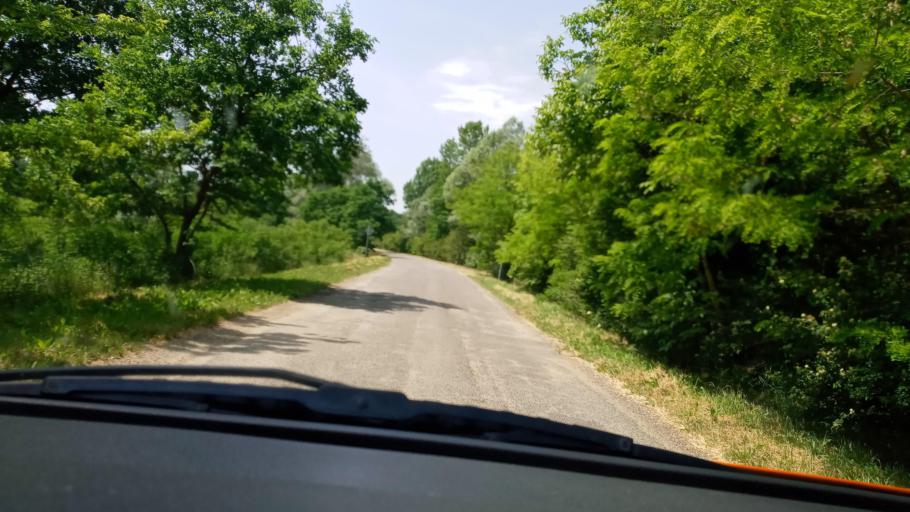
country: HU
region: Baranya
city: Sellye
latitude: 45.8088
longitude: 17.8698
